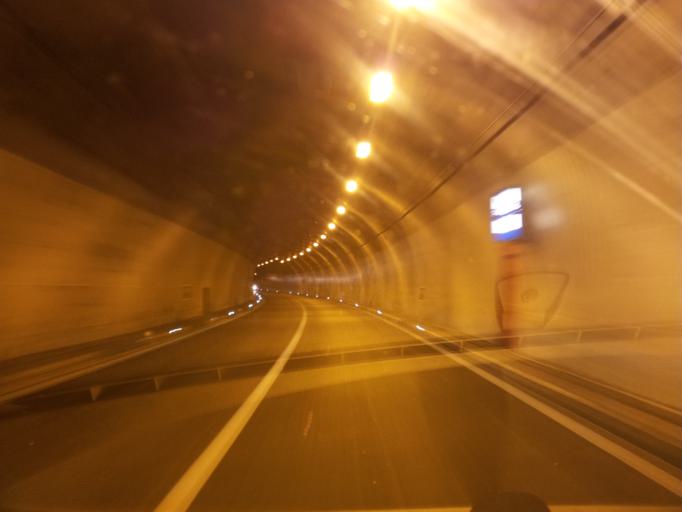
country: CH
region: Bern
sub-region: Interlaken-Oberhasli District
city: Ringgenberg
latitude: 46.7058
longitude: 7.9570
